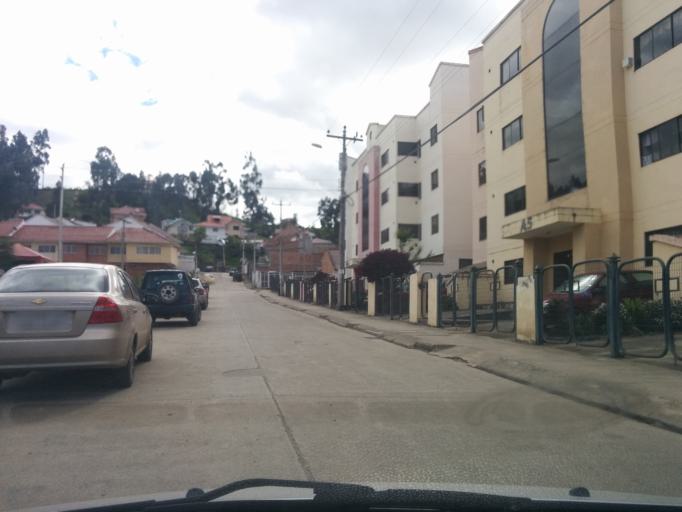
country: EC
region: Azuay
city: Cuenca
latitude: -2.9276
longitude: -79.0464
